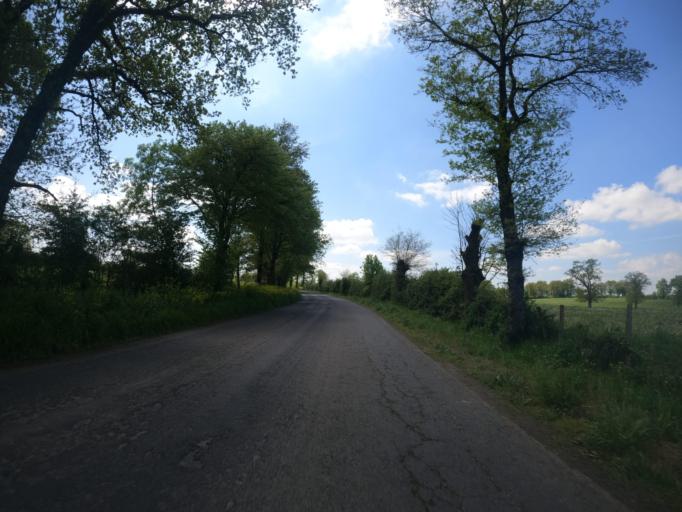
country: FR
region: Poitou-Charentes
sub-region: Departement des Deux-Sevres
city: Chiche
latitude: 46.7303
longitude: -0.3752
